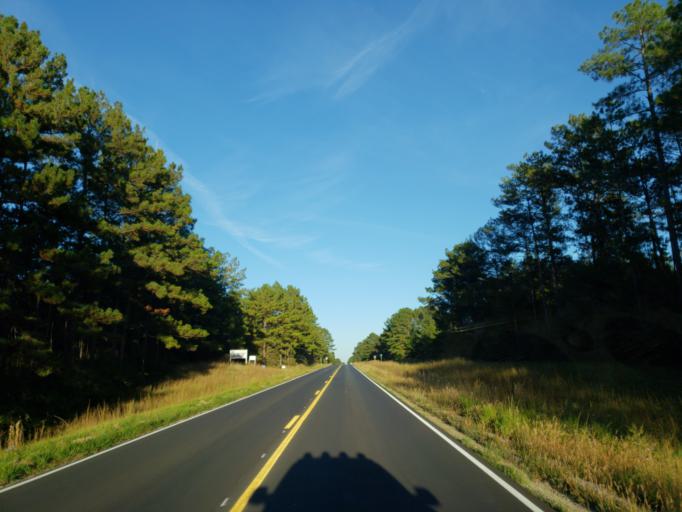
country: US
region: Mississippi
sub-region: Wayne County
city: Belmont
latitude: 31.4143
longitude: -88.5923
